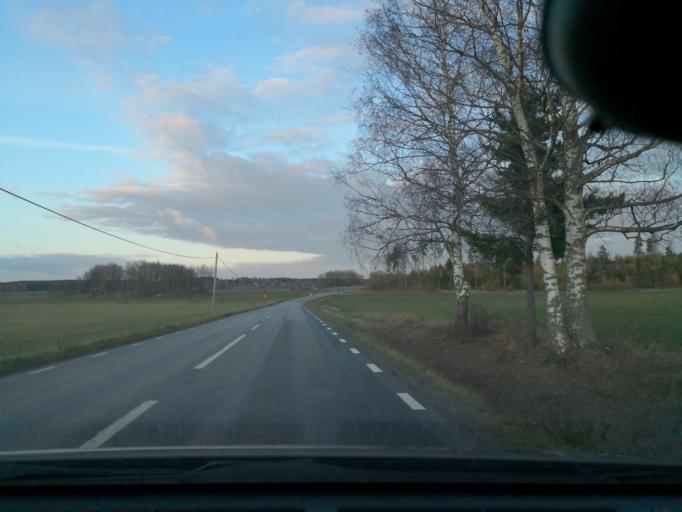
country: SE
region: Vaestmanland
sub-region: Vasteras
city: Tillberga
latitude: 59.6625
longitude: 16.7022
